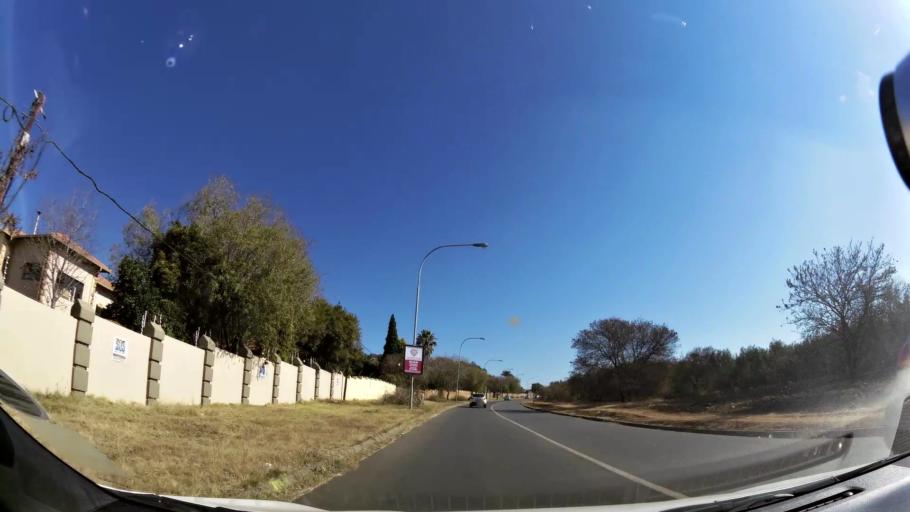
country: ZA
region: Gauteng
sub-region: City of Johannesburg Metropolitan Municipality
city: Johannesburg
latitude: -26.2918
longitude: 28.0705
